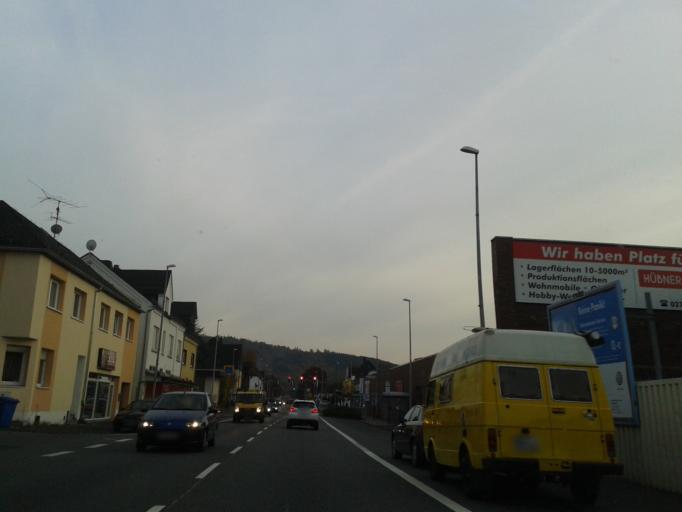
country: DE
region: Hesse
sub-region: Regierungsbezirk Giessen
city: Sinn
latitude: 50.6548
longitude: 8.3271
